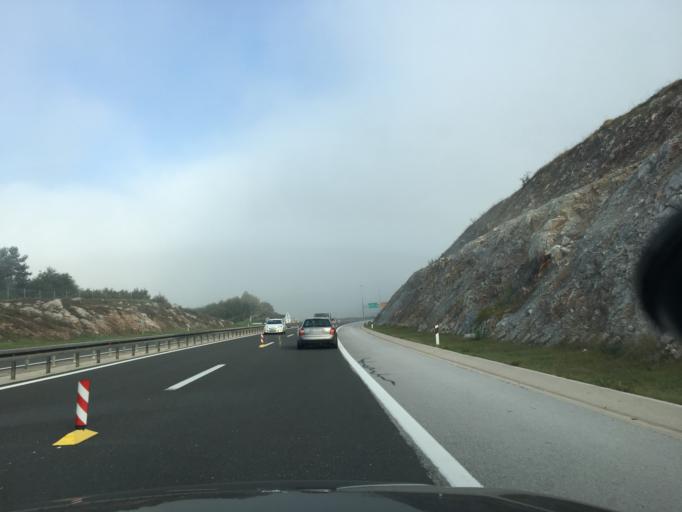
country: HR
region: Licko-Senjska
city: Otocac
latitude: 44.8858
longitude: 15.1962
